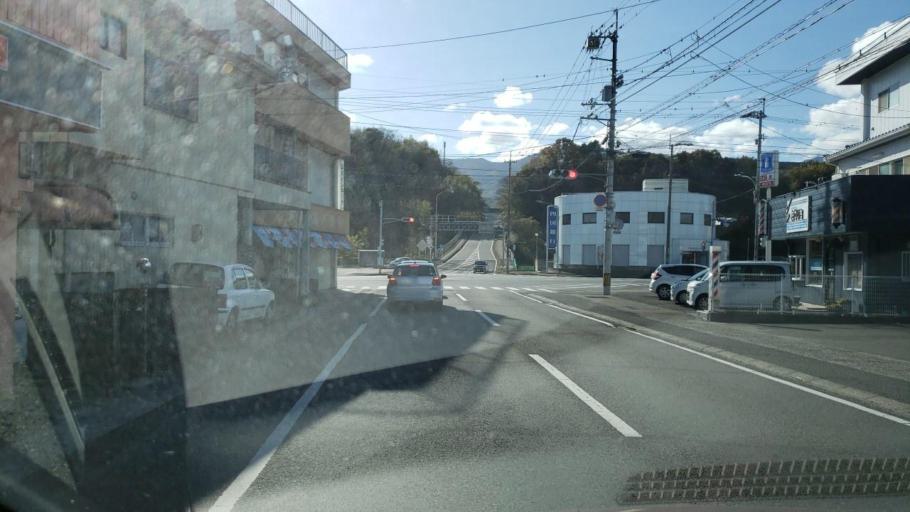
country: JP
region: Tokushima
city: Wakimachi
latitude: 34.0576
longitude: 134.2386
